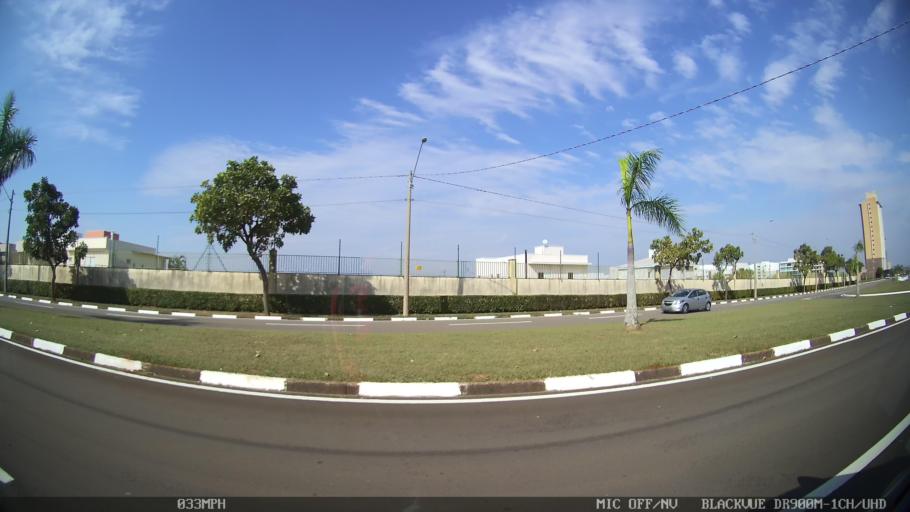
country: BR
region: Sao Paulo
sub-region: Paulinia
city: Paulinia
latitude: -22.7802
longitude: -47.1526
